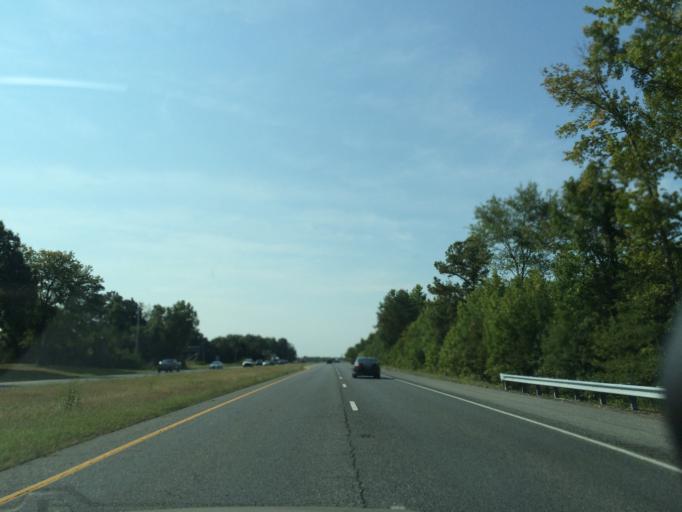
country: US
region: Maryland
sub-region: Charles County
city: La Plata
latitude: 38.4653
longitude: -76.9906
